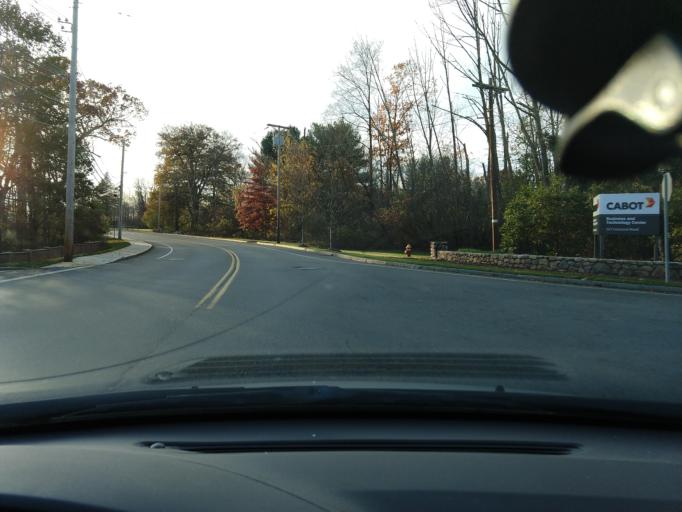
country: US
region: Massachusetts
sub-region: Middlesex County
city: Billerica
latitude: 42.5492
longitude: -71.2779
